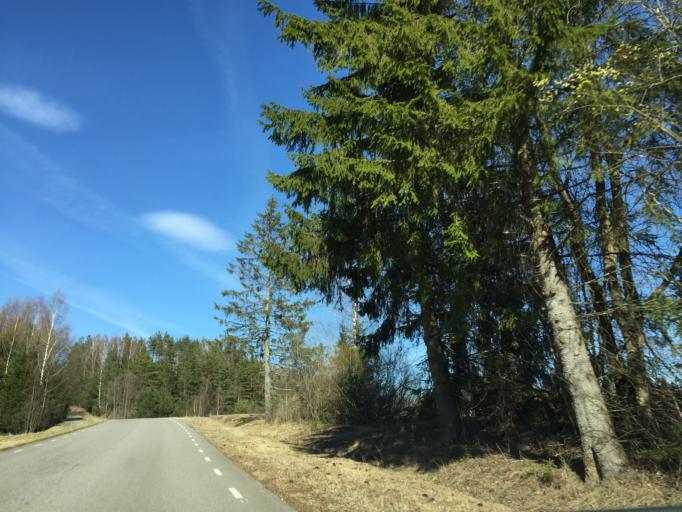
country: EE
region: Vorumaa
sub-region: Antsla vald
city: Vana-Antsla
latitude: 58.0224
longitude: 26.4691
